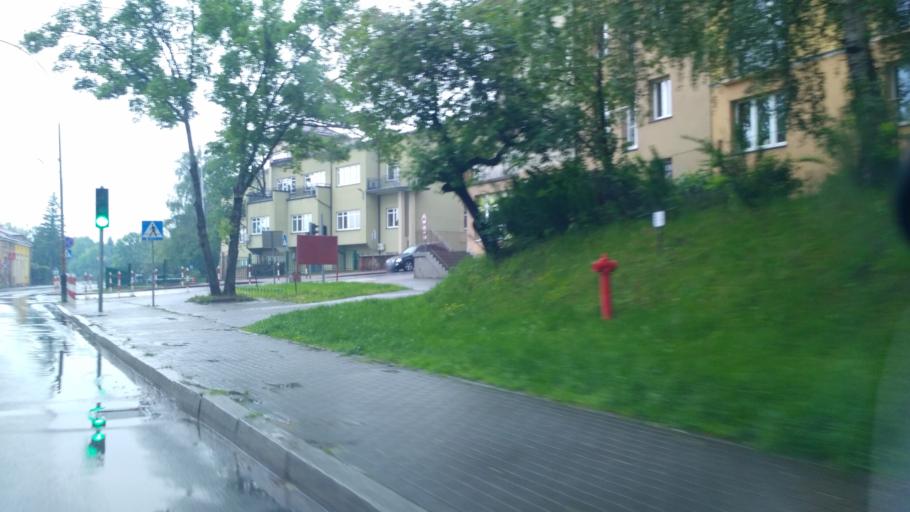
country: PL
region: Subcarpathian Voivodeship
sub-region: Powiat jasielski
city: Jaslo
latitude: 49.7456
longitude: 21.4678
